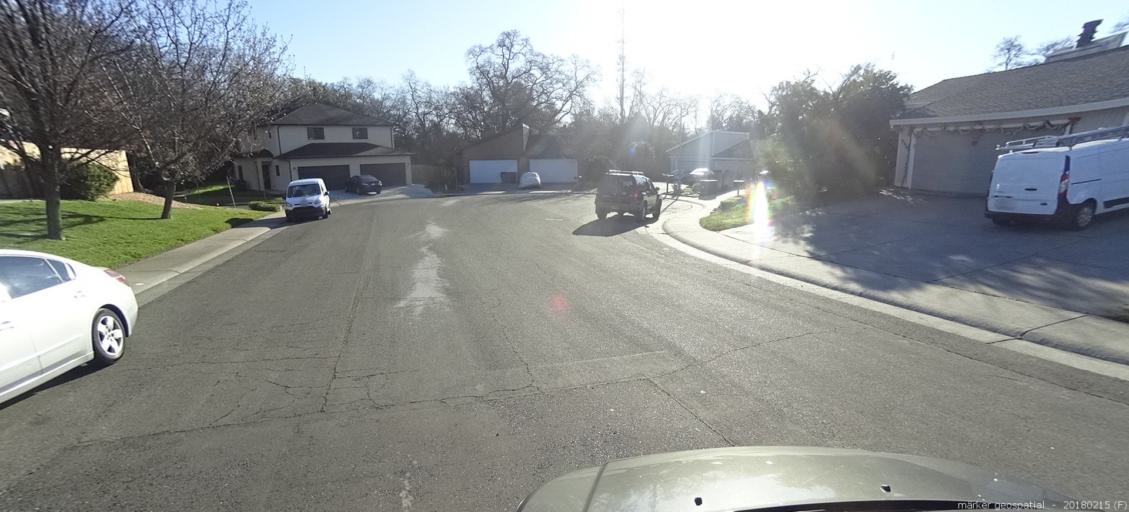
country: US
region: California
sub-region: Sacramento County
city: Foothill Farms
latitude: 38.6734
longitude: -121.3348
